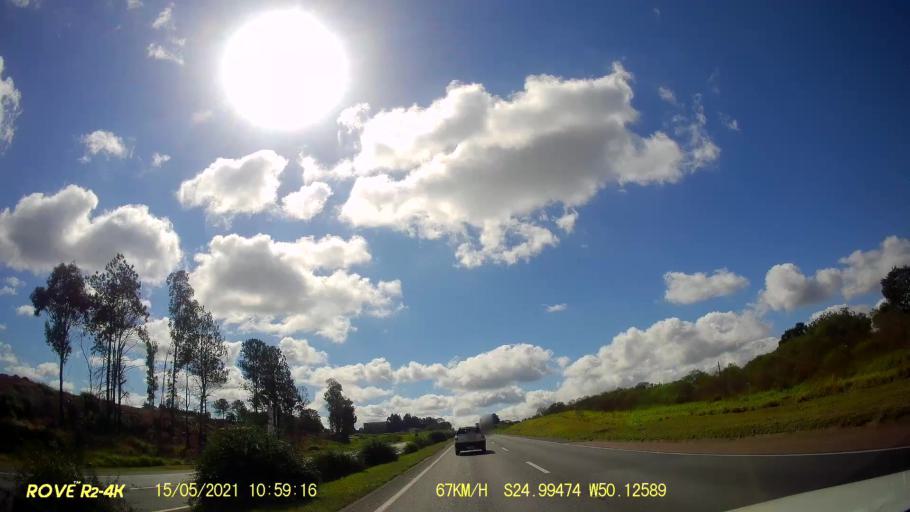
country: BR
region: Parana
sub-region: Carambei
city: Carambei
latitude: -24.9947
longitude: -50.1259
